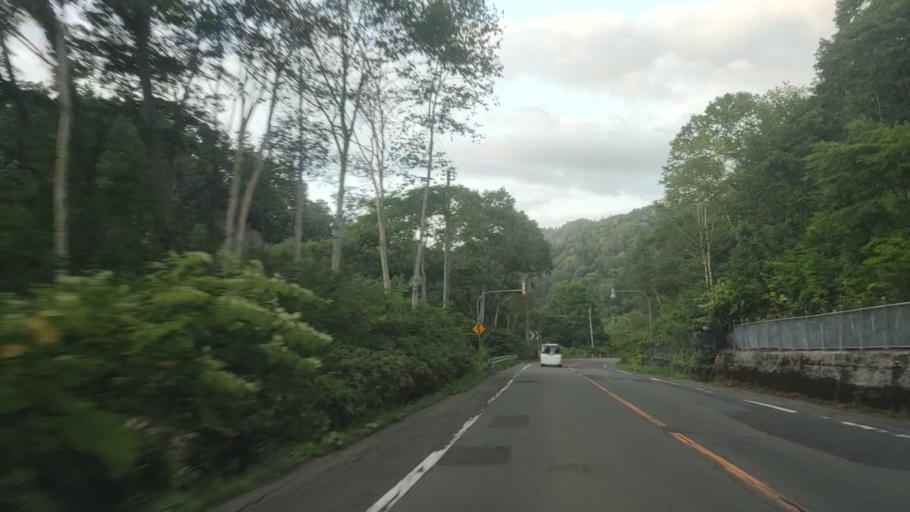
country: JP
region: Hokkaido
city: Utashinai
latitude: 43.2962
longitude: 142.0829
